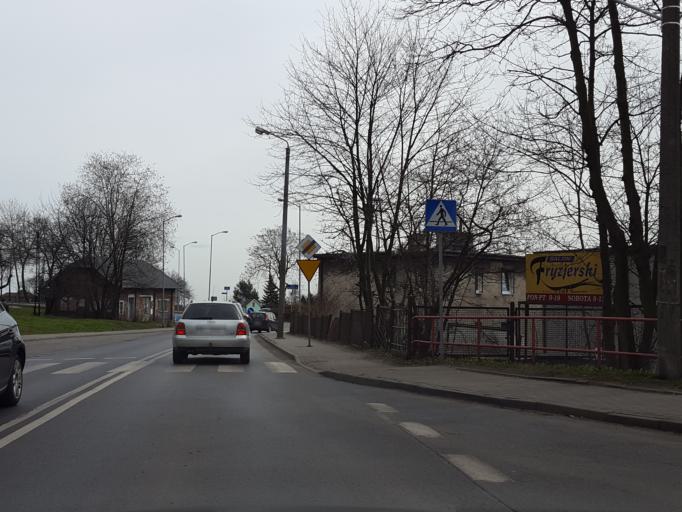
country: PL
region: Silesian Voivodeship
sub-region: Ruda Slaska
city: Ruda Slaska
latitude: 50.2714
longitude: 18.8729
